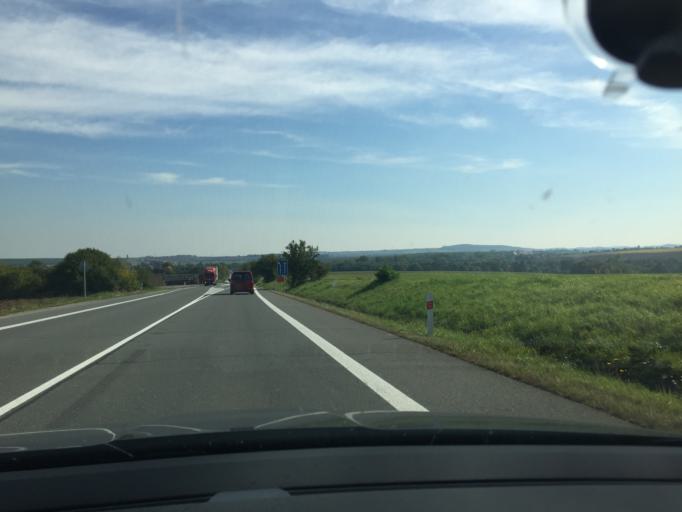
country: CZ
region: Central Bohemia
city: Planany
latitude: 50.0456
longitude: 15.0088
